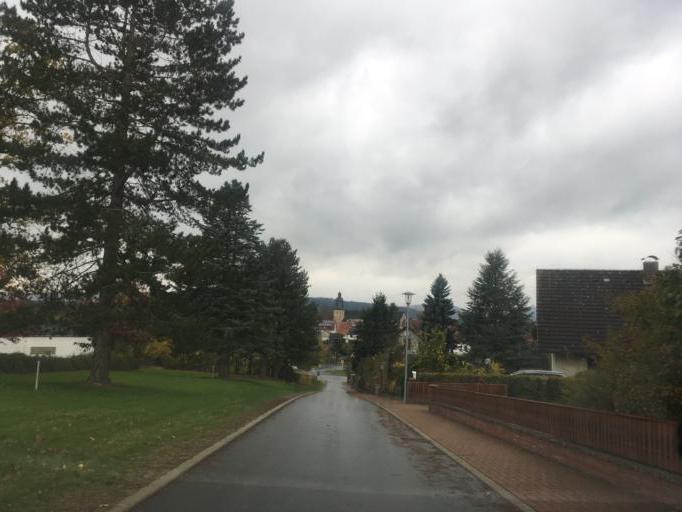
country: DE
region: Lower Saxony
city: Bodenfelde
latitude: 51.6218
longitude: 9.5600
